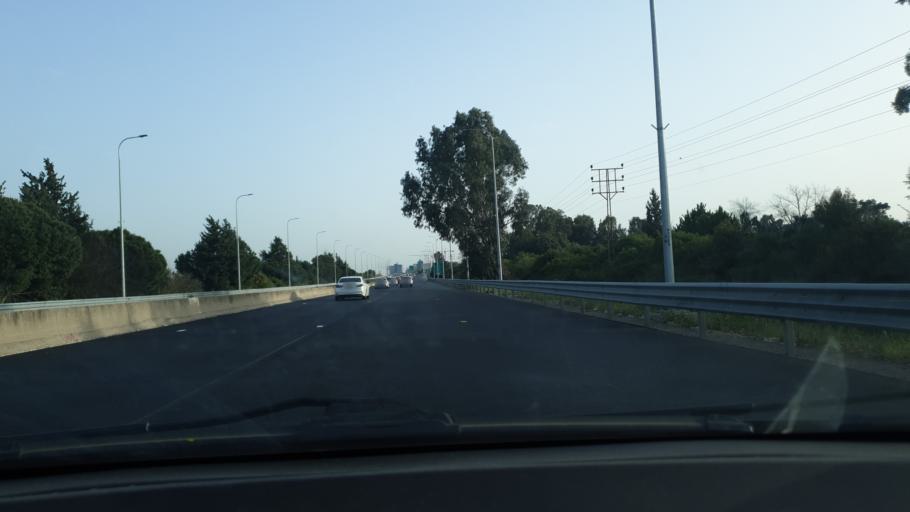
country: IL
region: Central District
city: Ra'anana
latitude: 32.2156
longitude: 34.8834
